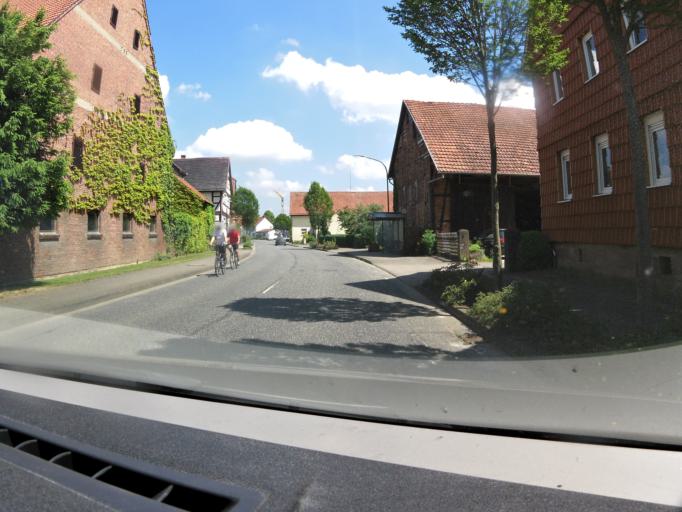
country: DE
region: Hesse
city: Breitenbach
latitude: 50.9377
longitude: 9.7752
